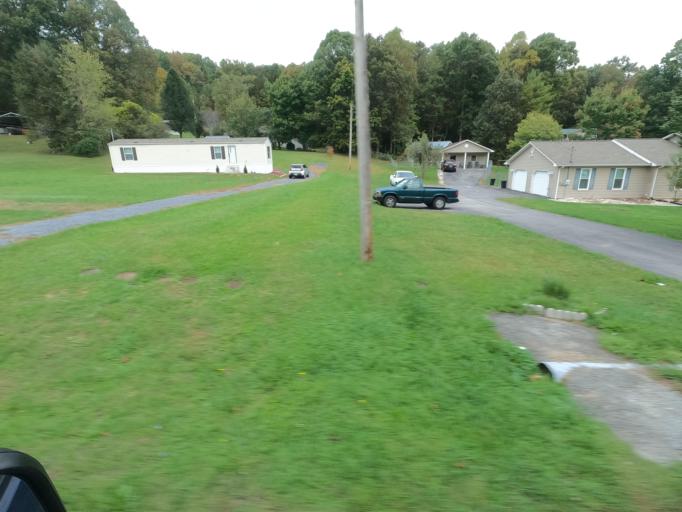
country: US
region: Tennessee
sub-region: Carter County
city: Elizabethton
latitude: 36.2628
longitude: -82.1994
